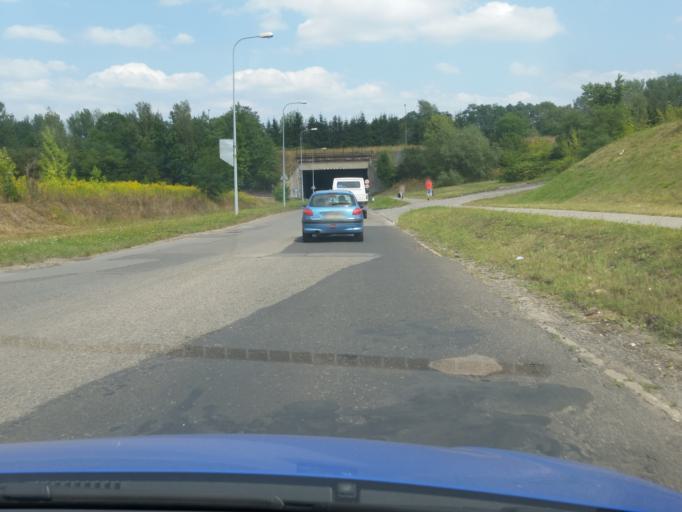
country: PL
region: Silesian Voivodeship
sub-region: Sosnowiec
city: Sosnowiec
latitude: 50.2507
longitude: 19.1217
